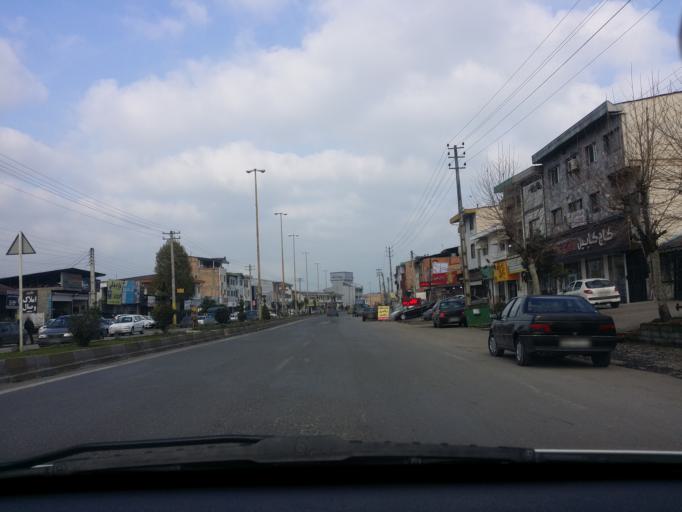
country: IR
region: Mazandaran
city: Chalus
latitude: 36.6773
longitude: 51.4039
